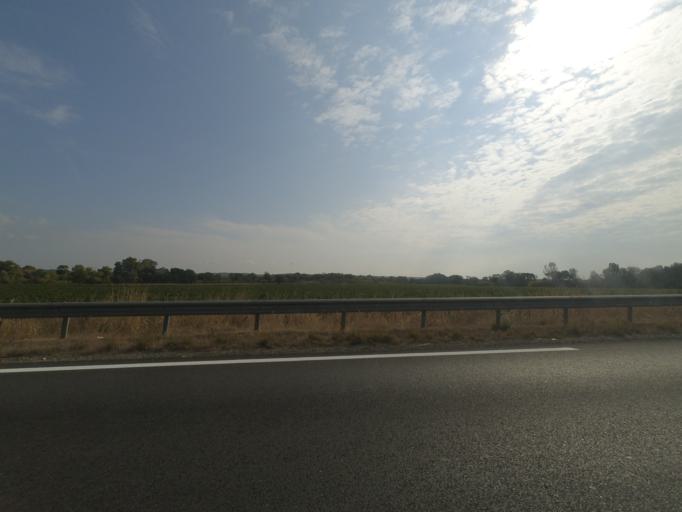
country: FR
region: Languedoc-Roussillon
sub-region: Departement de l'Herault
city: Boisseron
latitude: 43.7500
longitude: 4.0906
